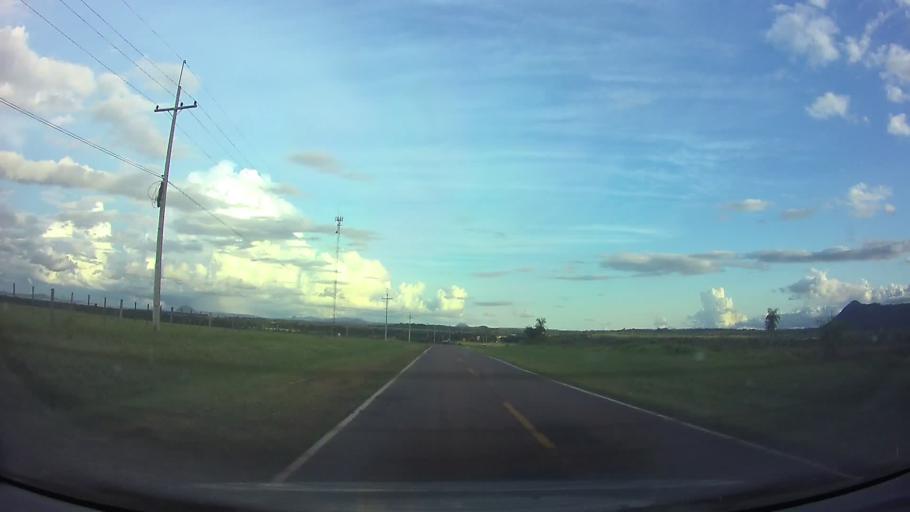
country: PY
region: Paraguari
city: Carapegua
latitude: -25.8274
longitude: -57.1612
